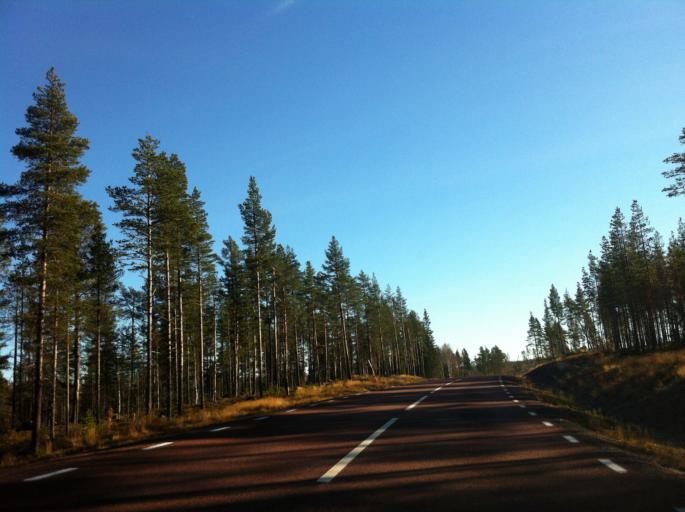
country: SE
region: Dalarna
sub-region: Alvdalens Kommun
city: AElvdalen
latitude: 61.6344
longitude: 13.2210
